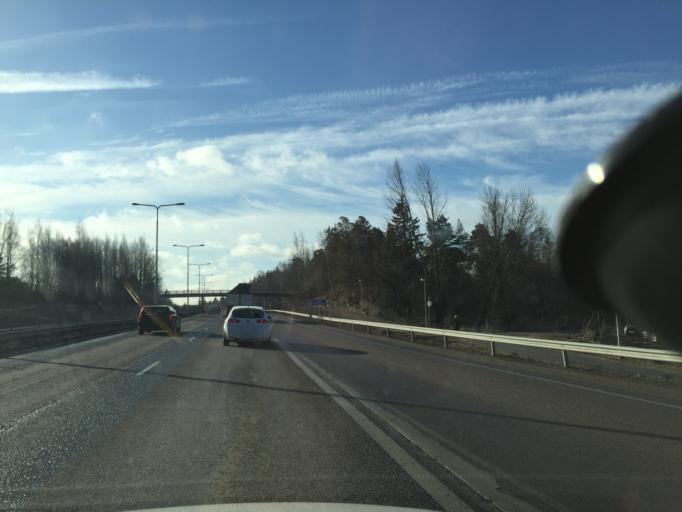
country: FI
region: Uusimaa
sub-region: Helsinki
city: Teekkarikylae
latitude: 60.2614
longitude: 24.8763
